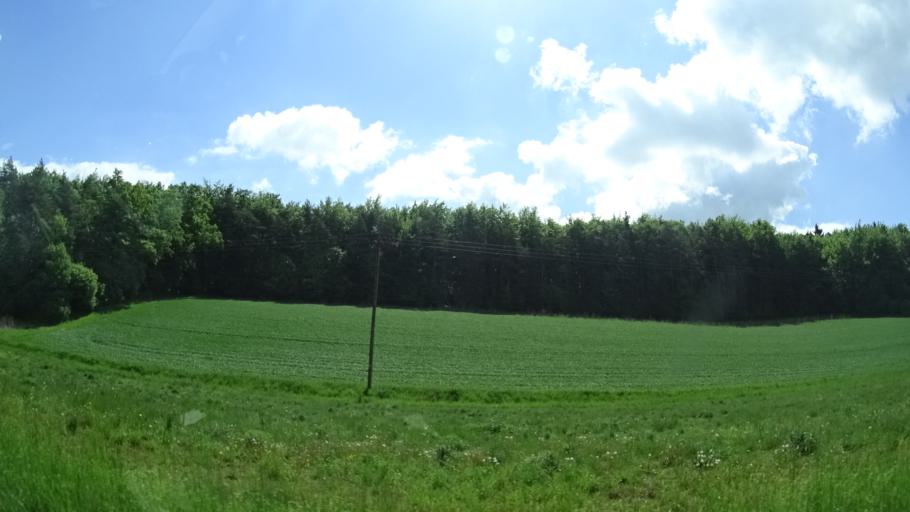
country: DE
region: Bavaria
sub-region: Regierungsbezirk Unterfranken
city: Bastheim
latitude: 50.4211
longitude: 10.2335
